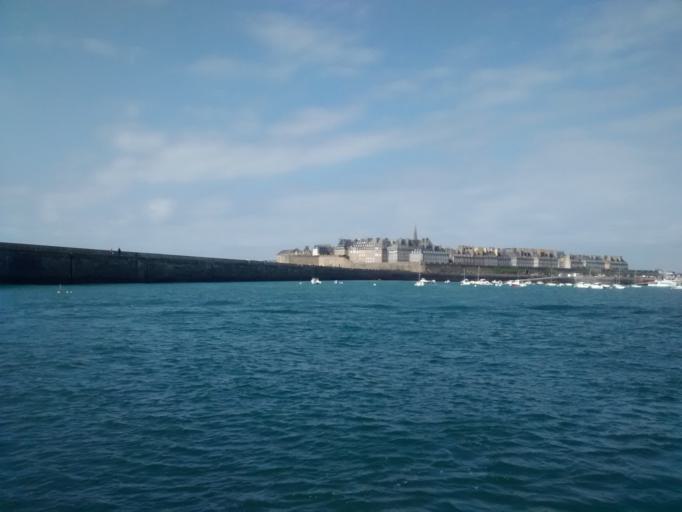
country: FR
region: Brittany
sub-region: Departement d'Ille-et-Vilaine
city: Saint-Malo
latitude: 48.6413
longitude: -2.0311
